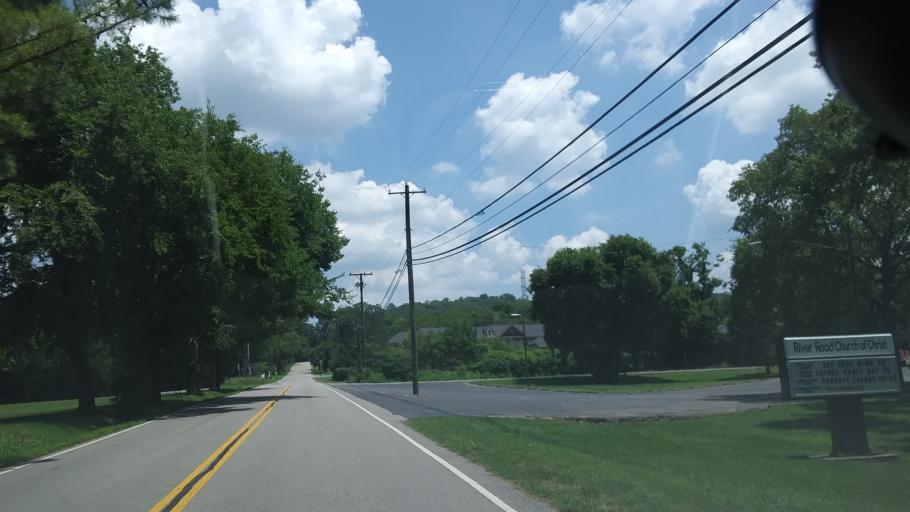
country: US
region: Tennessee
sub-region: Davidson County
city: Belle Meade
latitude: 36.1219
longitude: -86.9251
